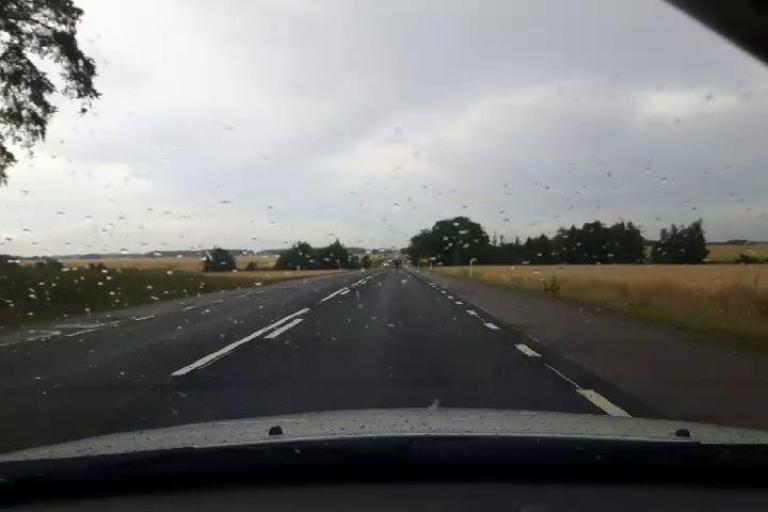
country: SE
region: Uppsala
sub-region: Osthammars Kommun
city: Bjorklinge
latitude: 59.9599
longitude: 17.5838
